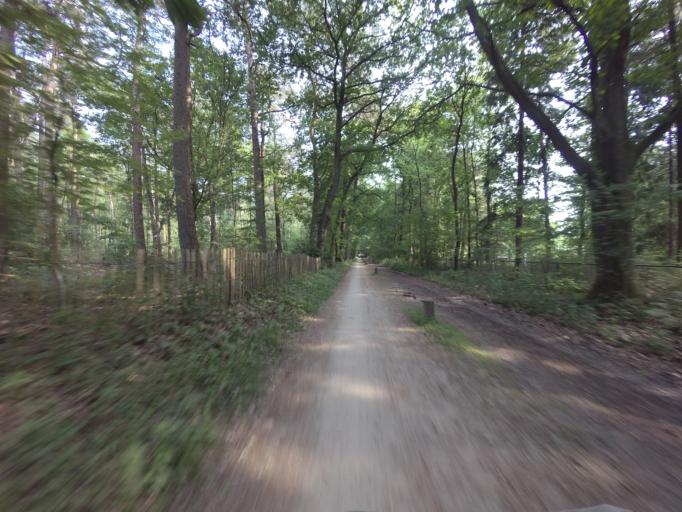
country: NL
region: North Holland
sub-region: Gemeente Hilversum
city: Hilversum
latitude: 52.1803
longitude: 5.1947
